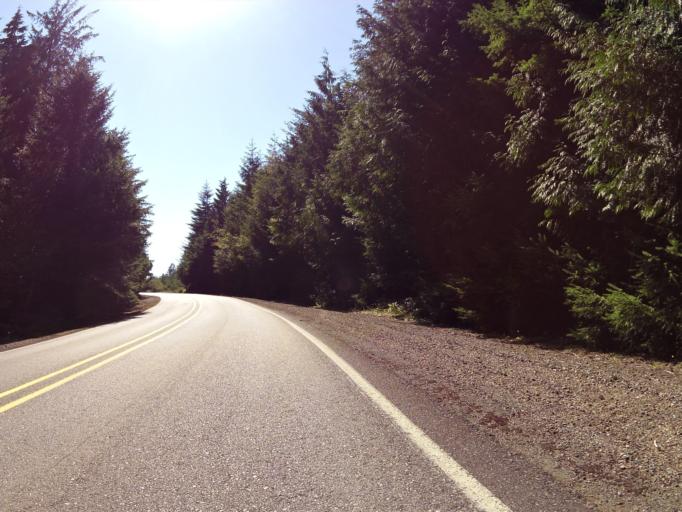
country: US
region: Oregon
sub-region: Coos County
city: Barview
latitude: 43.2405
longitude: -124.3387
